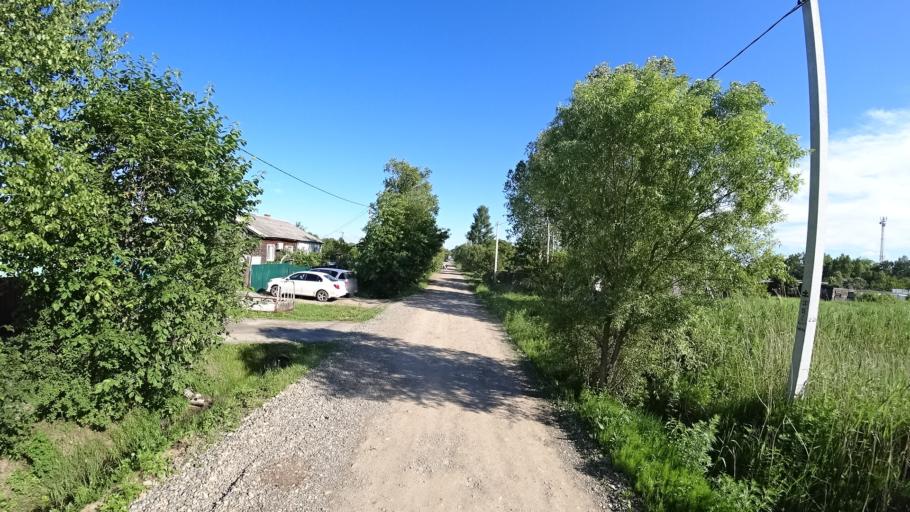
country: RU
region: Khabarovsk Krai
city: Khor
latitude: 47.8944
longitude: 134.9936
